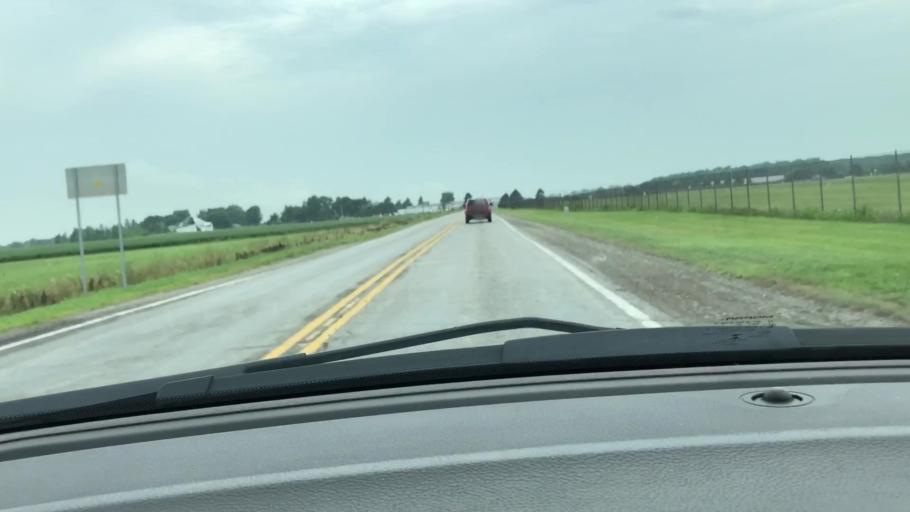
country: US
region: Michigan
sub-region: Saginaw County
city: Freeland
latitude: 43.5220
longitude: -84.0913
